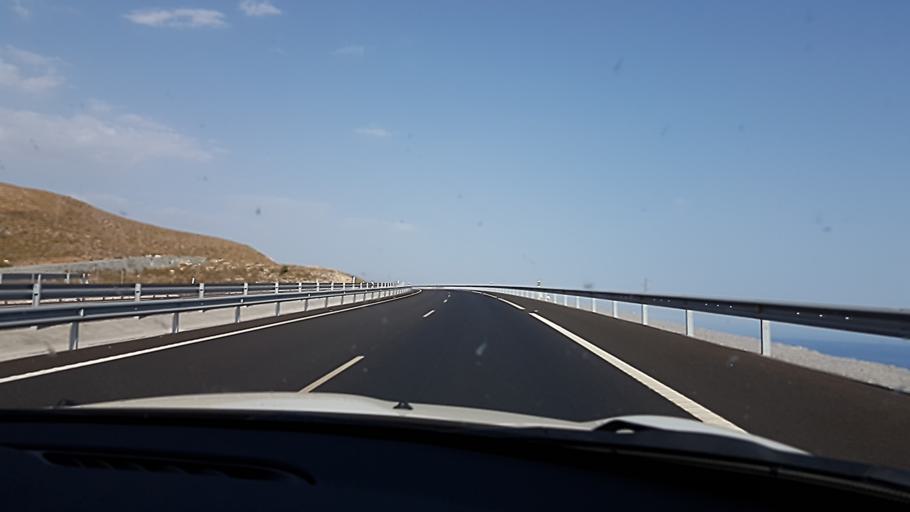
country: ES
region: Andalusia
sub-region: Provincia de Granada
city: Gualchos
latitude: 36.7155
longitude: -3.3847
